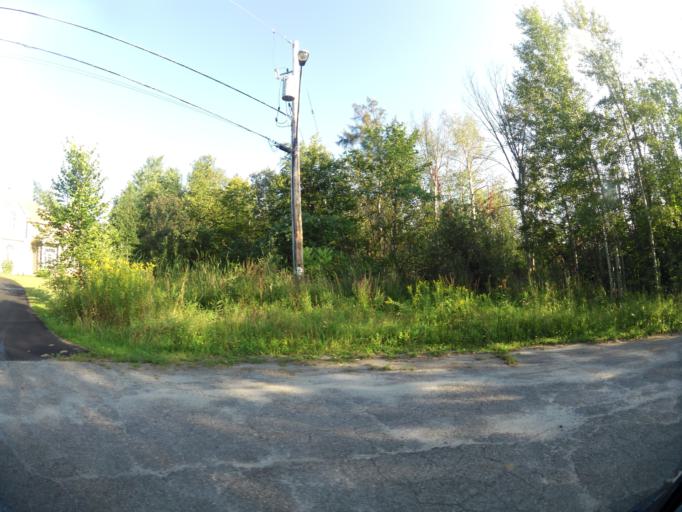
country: CA
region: Ontario
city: Clarence-Rockland
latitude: 45.4981
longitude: -75.4488
